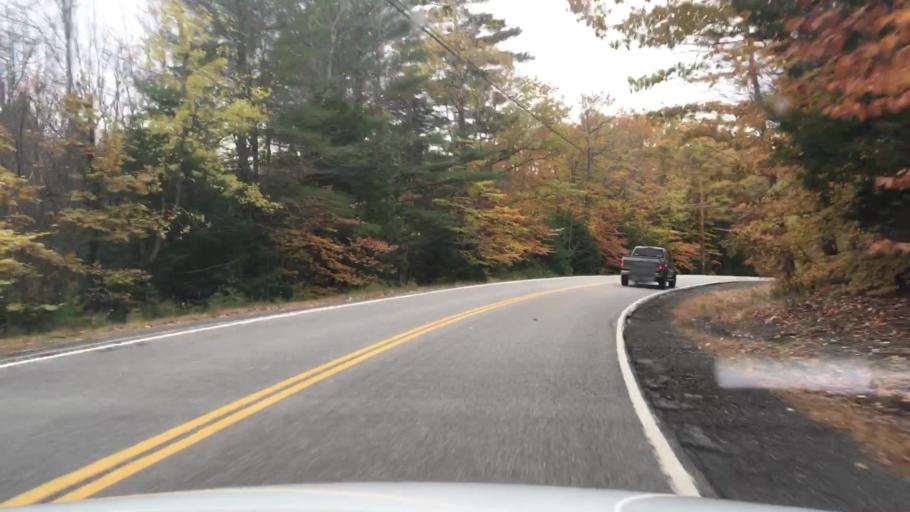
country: US
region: Maine
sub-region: Androscoggin County
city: Sabattus
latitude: 44.1306
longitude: -70.0472
